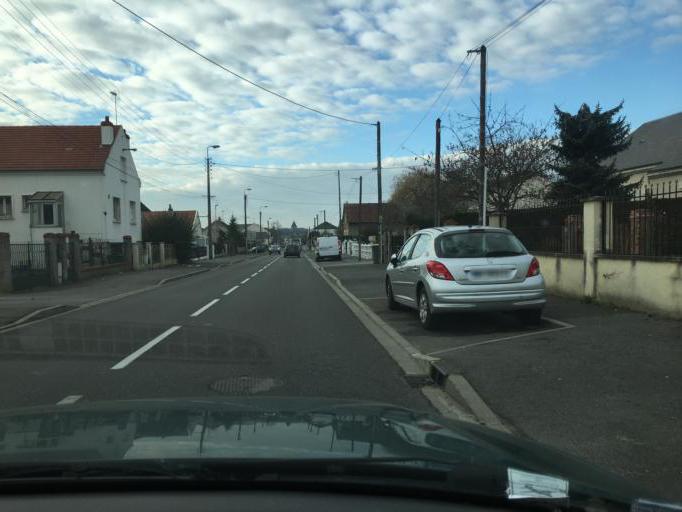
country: FR
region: Centre
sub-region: Departement du Loiret
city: Saran
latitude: 47.9514
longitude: 1.8848
